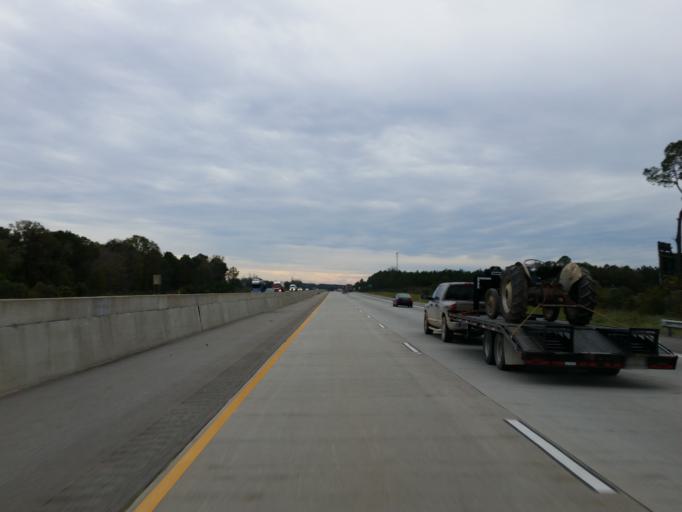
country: US
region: Georgia
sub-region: Tift County
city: Unionville
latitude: 31.3318
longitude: -83.4830
